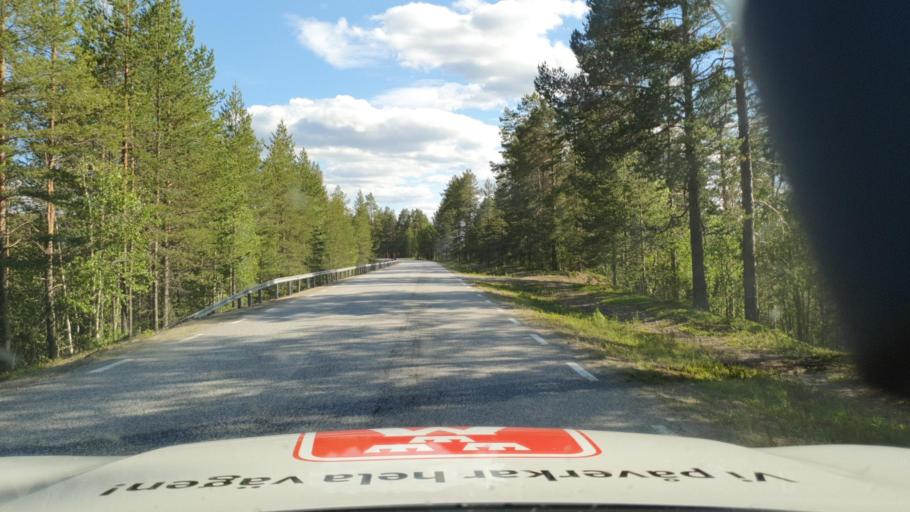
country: SE
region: Vaesterbotten
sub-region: Skelleftea Kommun
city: Langsele
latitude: 64.7798
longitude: 20.0180
